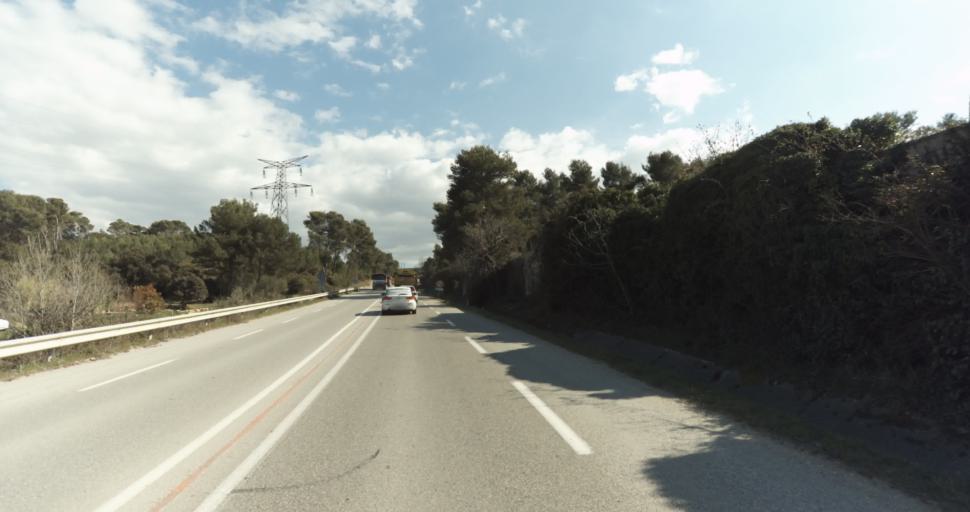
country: FR
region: Provence-Alpes-Cote d'Azur
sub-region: Departement des Bouches-du-Rhone
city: Gardanne
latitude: 43.4587
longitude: 5.4901
